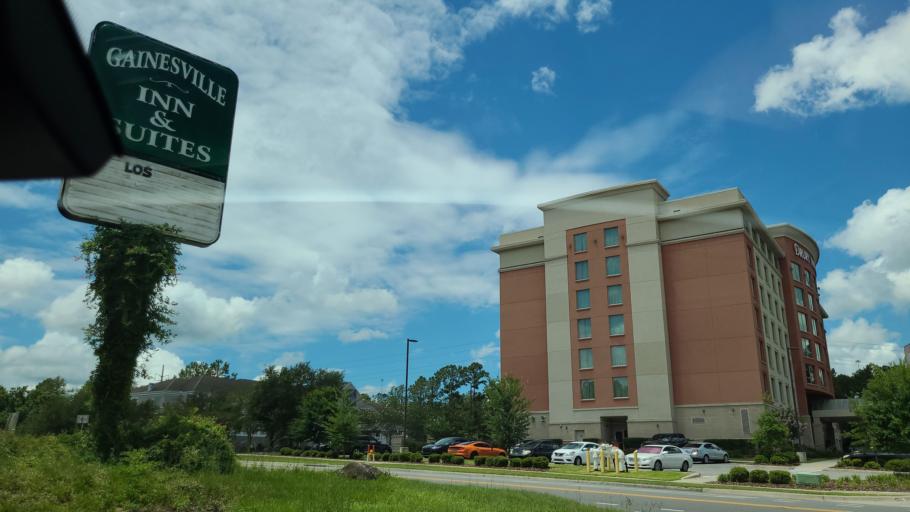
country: US
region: Florida
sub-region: Alachua County
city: Gainesville
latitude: 29.6174
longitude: -82.3830
